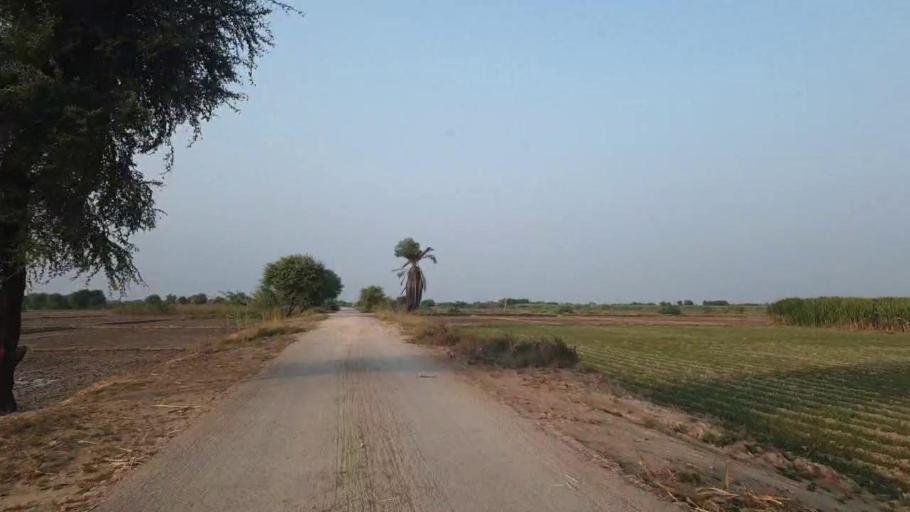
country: PK
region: Sindh
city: Tando Ghulam Ali
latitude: 25.0749
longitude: 68.9595
